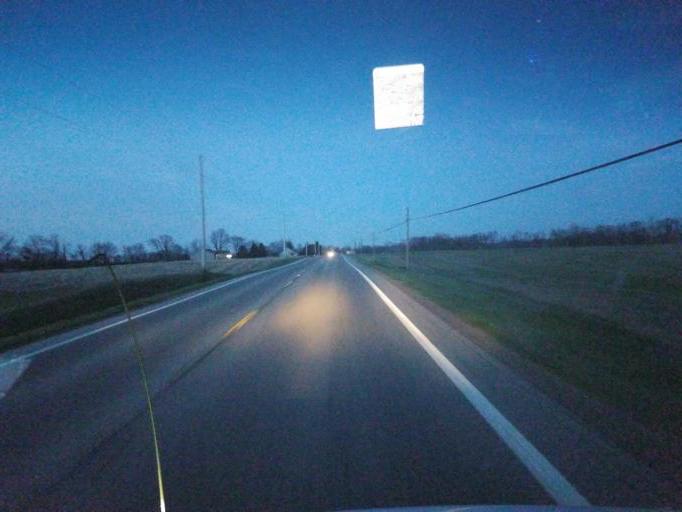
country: US
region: Ohio
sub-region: Logan County
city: De Graff
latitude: 40.3588
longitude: -83.8803
